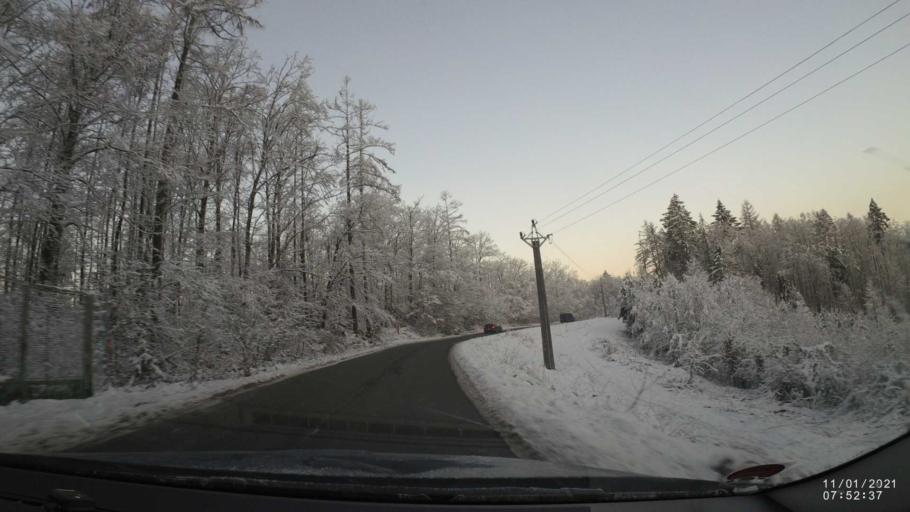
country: CZ
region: South Moravian
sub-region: Okres Blansko
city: Adamov
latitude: 49.2877
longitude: 16.6421
